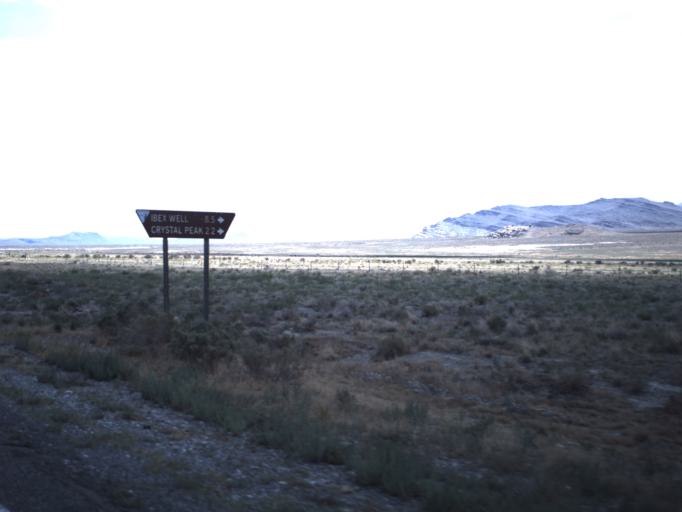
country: US
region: Utah
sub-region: Beaver County
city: Milford
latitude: 39.0421
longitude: -113.4037
